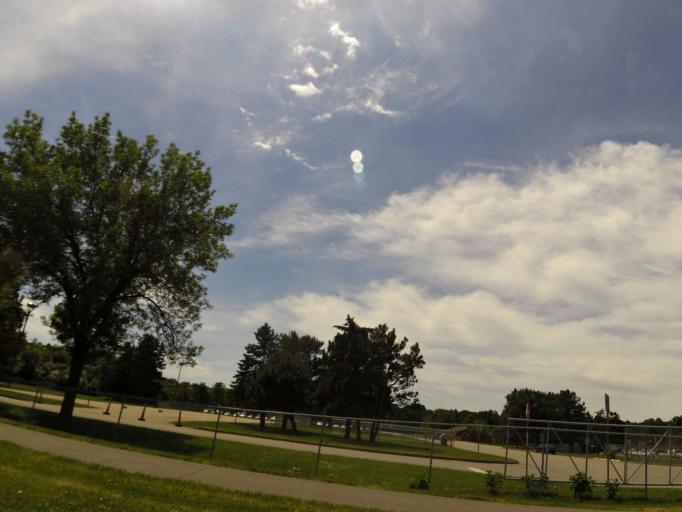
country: US
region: Minnesota
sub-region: Dakota County
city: Eagan
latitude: 44.7901
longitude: -93.2123
